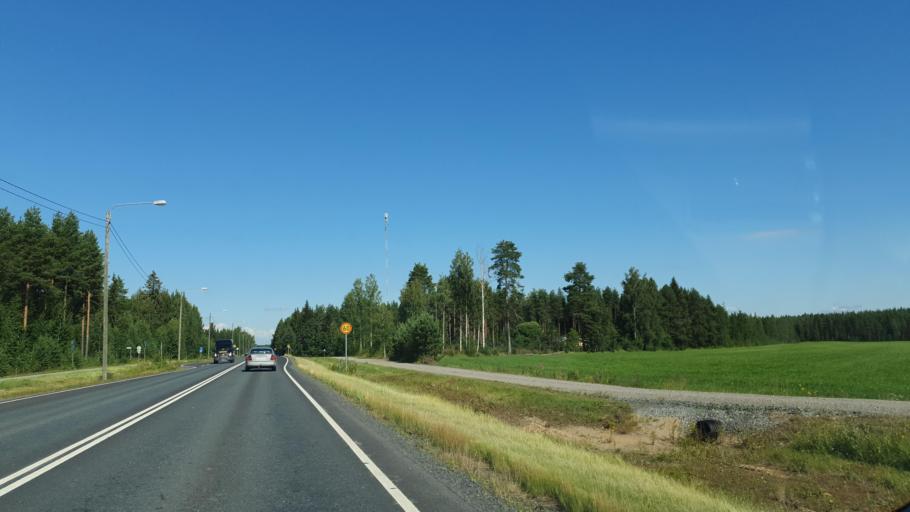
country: FI
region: Northern Savo
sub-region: Ylae-Savo
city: Lapinlahti
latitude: 63.4240
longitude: 27.3302
